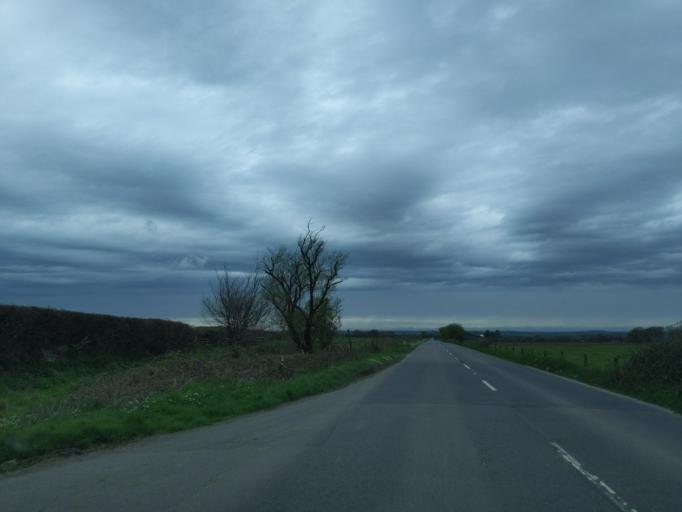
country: GB
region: England
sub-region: Devon
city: Winkleigh
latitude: 50.9110
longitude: -4.0247
